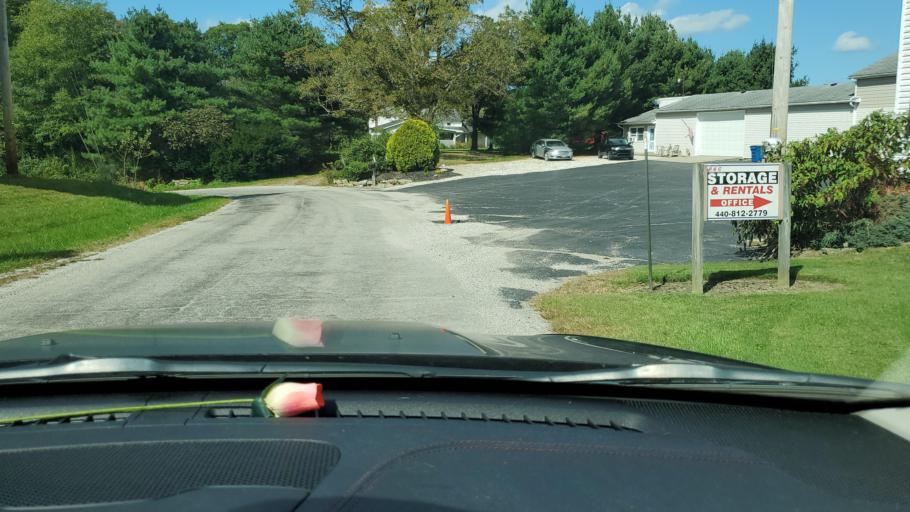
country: US
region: Ohio
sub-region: Ashtabula County
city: Andover
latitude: 41.4641
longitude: -80.5661
